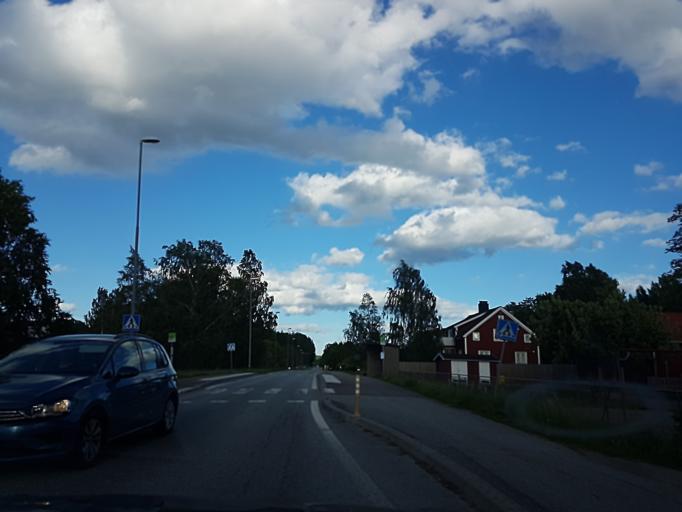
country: SE
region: Soedermanland
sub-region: Nykopings Kommun
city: Svalsta
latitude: 58.7415
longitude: 16.9182
